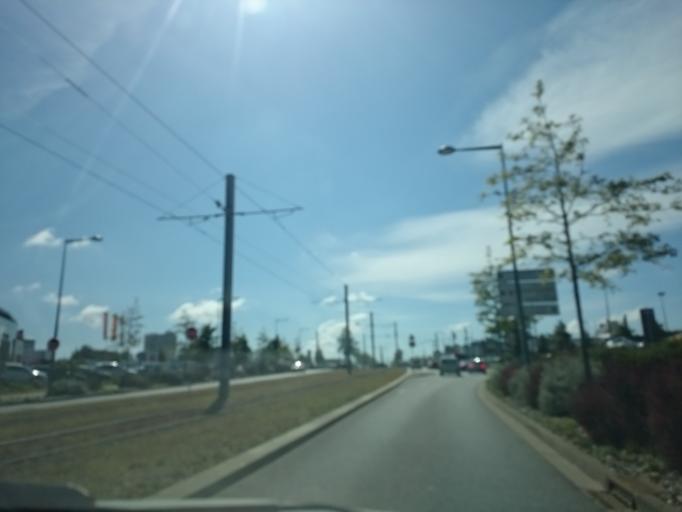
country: FR
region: Brittany
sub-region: Departement du Finistere
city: Brest
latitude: 48.4164
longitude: -4.4664
